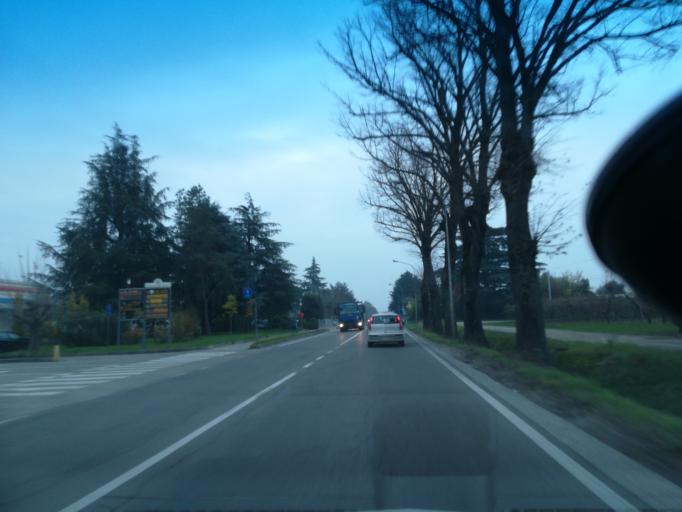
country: IT
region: Emilia-Romagna
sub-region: Provincia di Ravenna
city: Castel Bolognese
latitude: 44.3245
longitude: 11.7873
